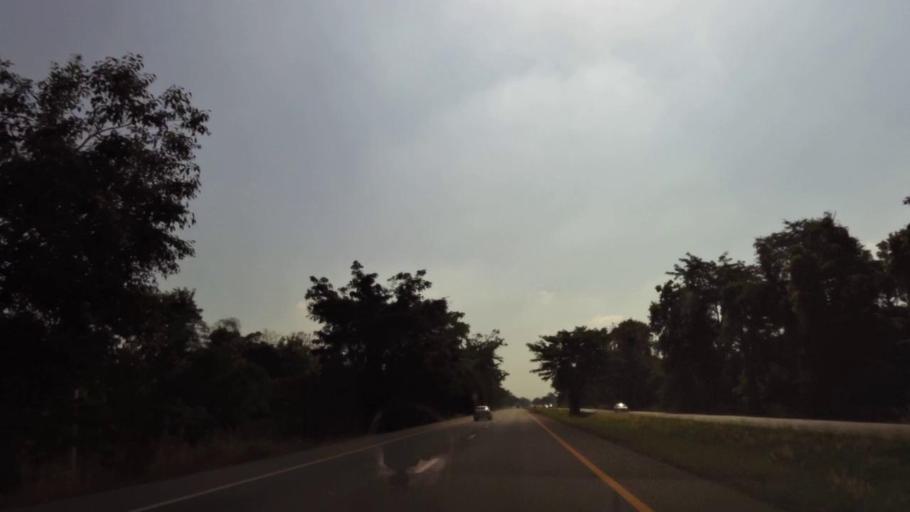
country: TH
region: Phichit
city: Bueng Na Rang
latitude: 16.2005
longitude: 100.1280
